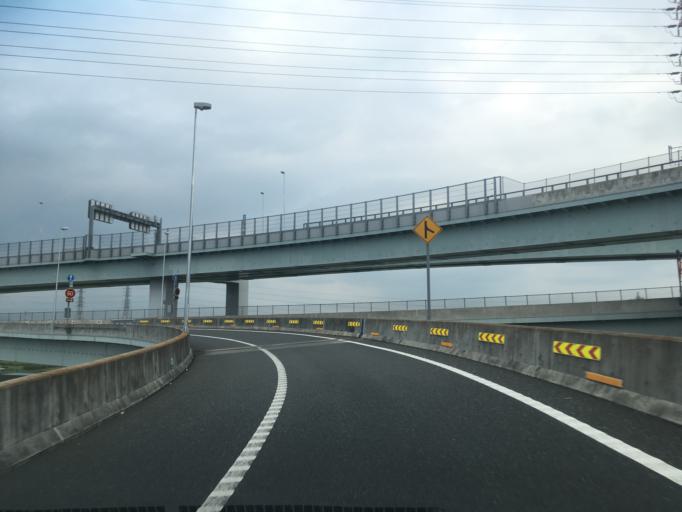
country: JP
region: Kanagawa
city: Chigasaki
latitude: 35.3501
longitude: 139.3922
